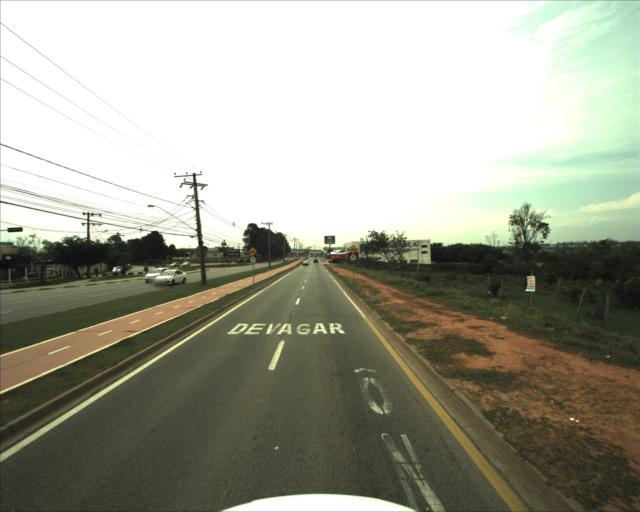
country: BR
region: Sao Paulo
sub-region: Sorocaba
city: Sorocaba
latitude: -23.4508
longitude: -47.4410
